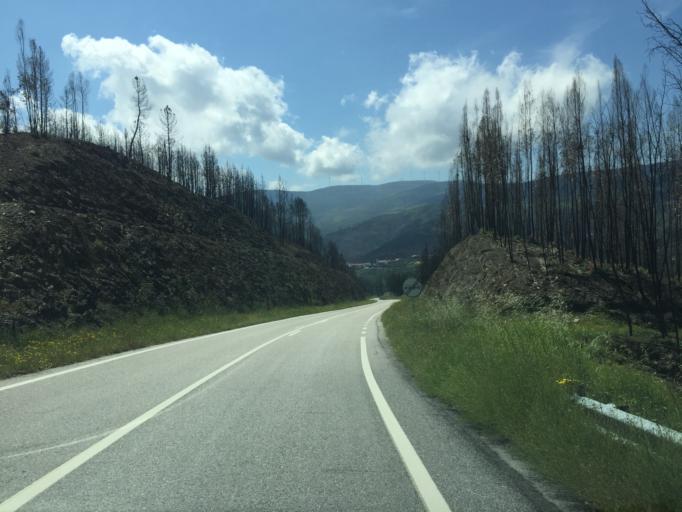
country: PT
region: Coimbra
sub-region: Pampilhosa da Serra
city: Pampilhosa da Serra
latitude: 39.9895
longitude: -7.9684
